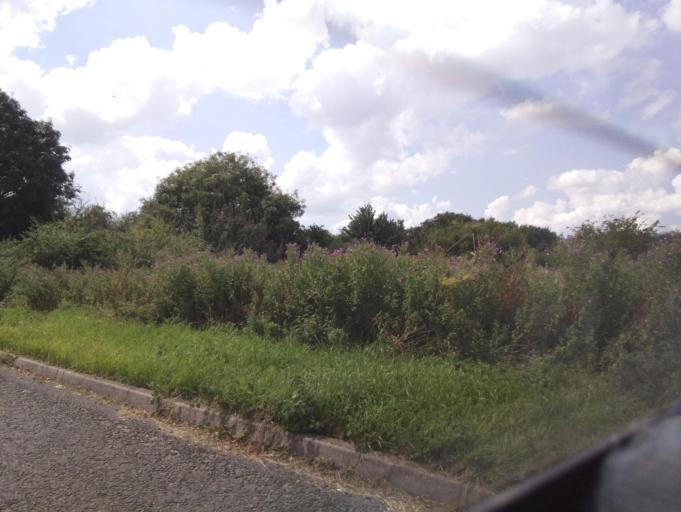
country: GB
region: England
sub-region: Wiltshire
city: Lydiard Tregoze
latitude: 51.5733
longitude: -1.8355
